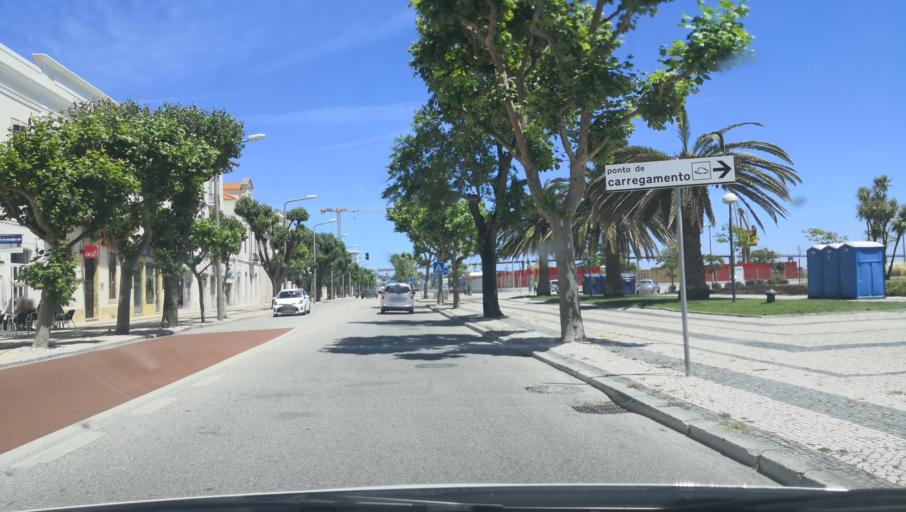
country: PT
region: Coimbra
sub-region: Figueira da Foz
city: Figueira da Foz
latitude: 40.1480
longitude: -8.8547
